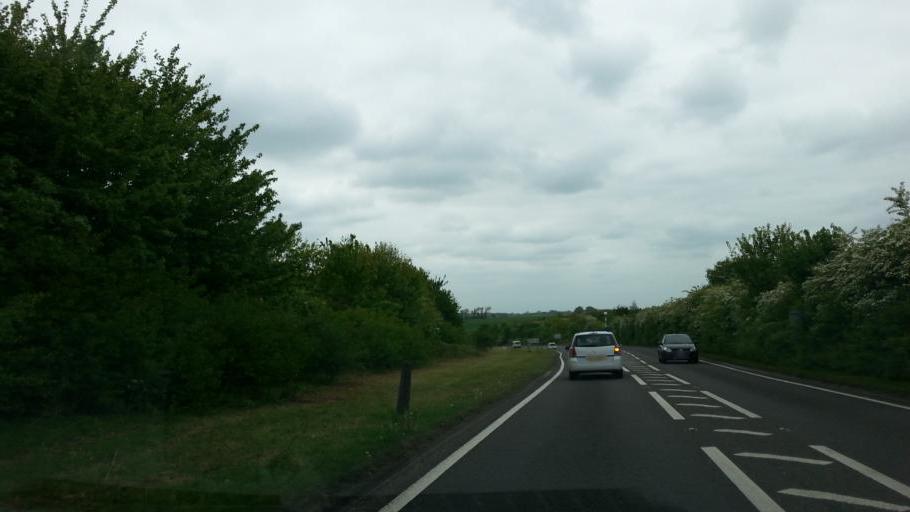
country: GB
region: England
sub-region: Suffolk
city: Hadleigh
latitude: 52.0540
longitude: 0.9673
